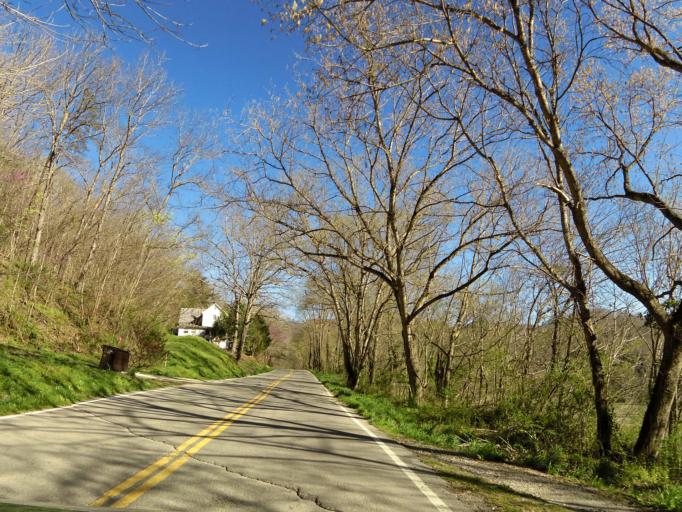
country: US
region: Tennessee
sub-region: Scott County
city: Huntsville
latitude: 36.3337
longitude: -84.3828
